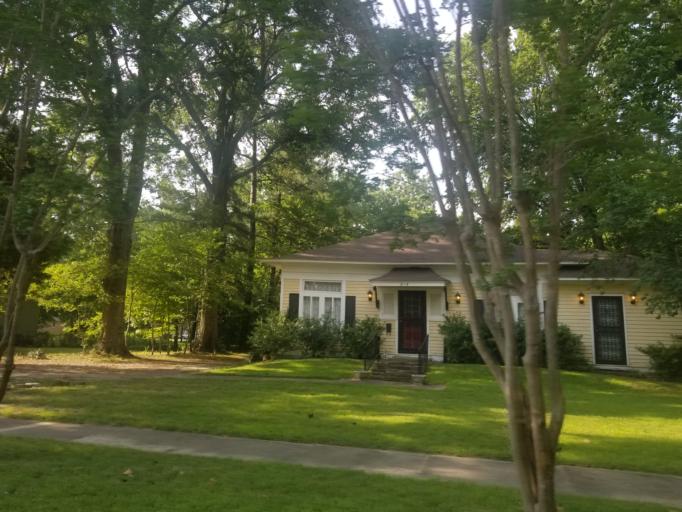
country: US
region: Arkansas
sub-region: Cross County
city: Wynne
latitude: 35.2256
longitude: -90.7838
